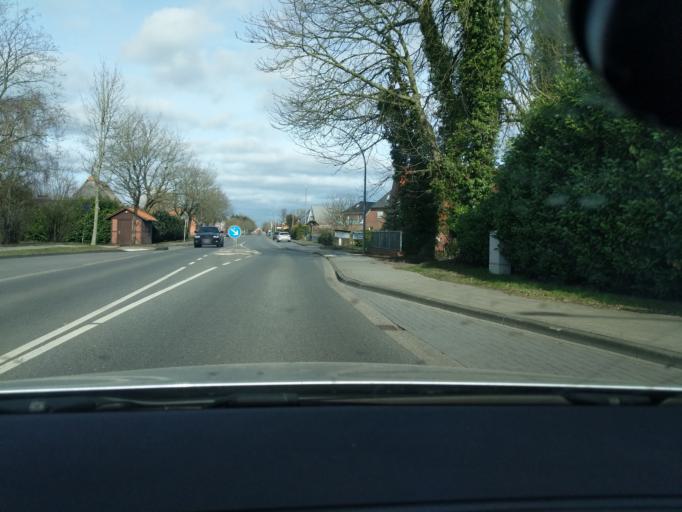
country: DE
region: Lower Saxony
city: Stade
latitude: 53.6441
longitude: 9.4800
